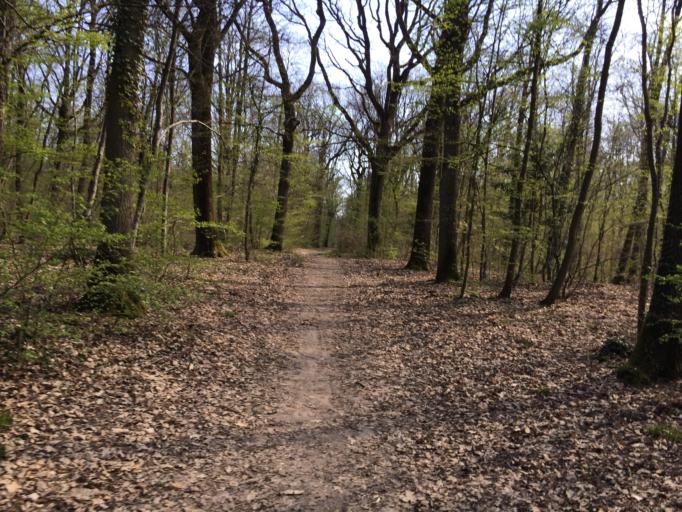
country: FR
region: Ile-de-France
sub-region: Departement de l'Essonne
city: Draveil
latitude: 48.6716
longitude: 2.4175
